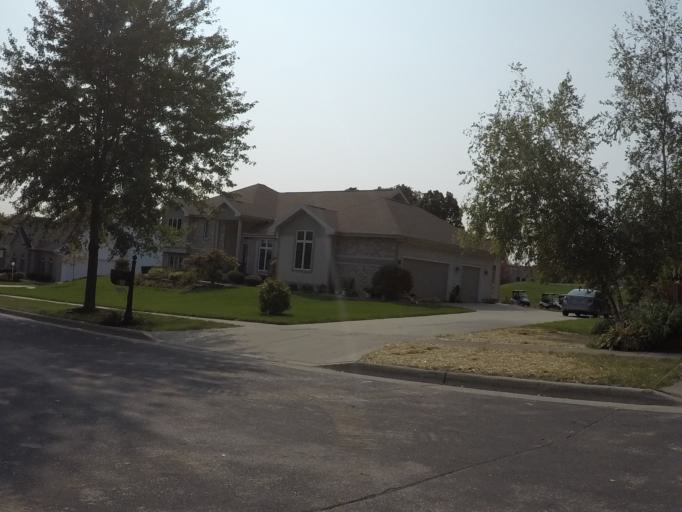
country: US
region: Wisconsin
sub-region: Dane County
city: Verona
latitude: 43.0369
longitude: -89.5377
